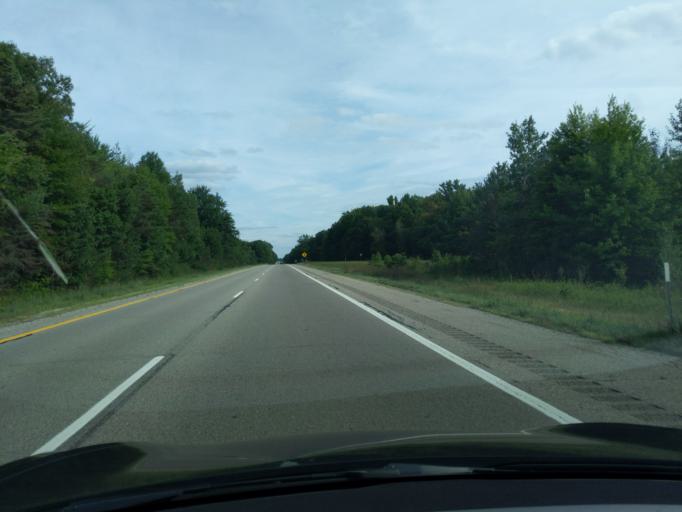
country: US
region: Michigan
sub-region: Muskegon County
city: Fruitport
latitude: 43.1204
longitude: -86.1329
